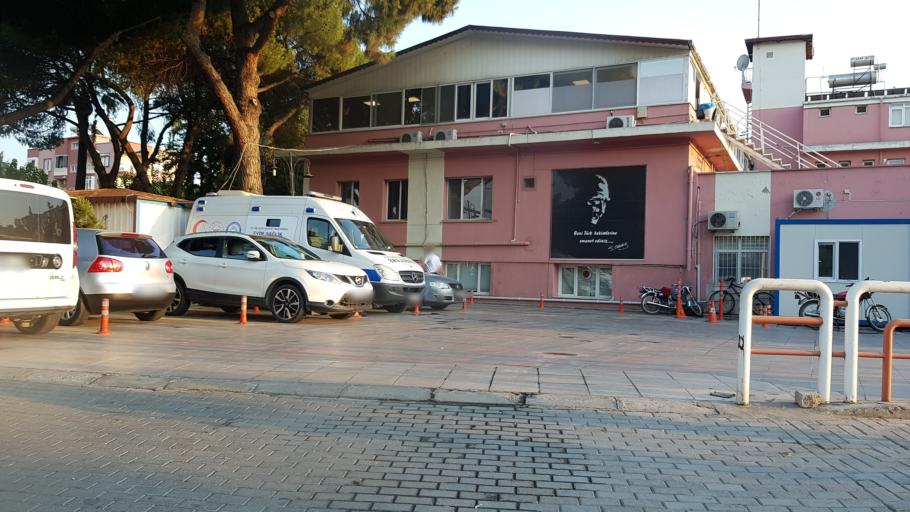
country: TR
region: Izmir
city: Selcuk
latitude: 37.9479
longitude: 27.3678
